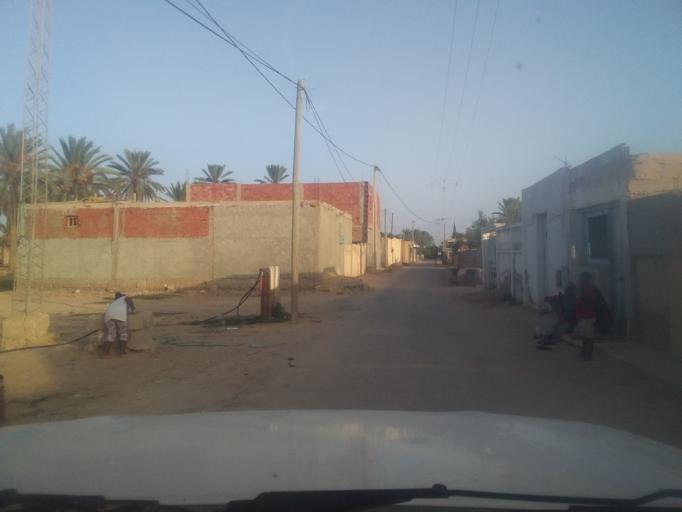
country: TN
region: Qabis
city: Gabes
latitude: 33.6224
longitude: 10.2952
